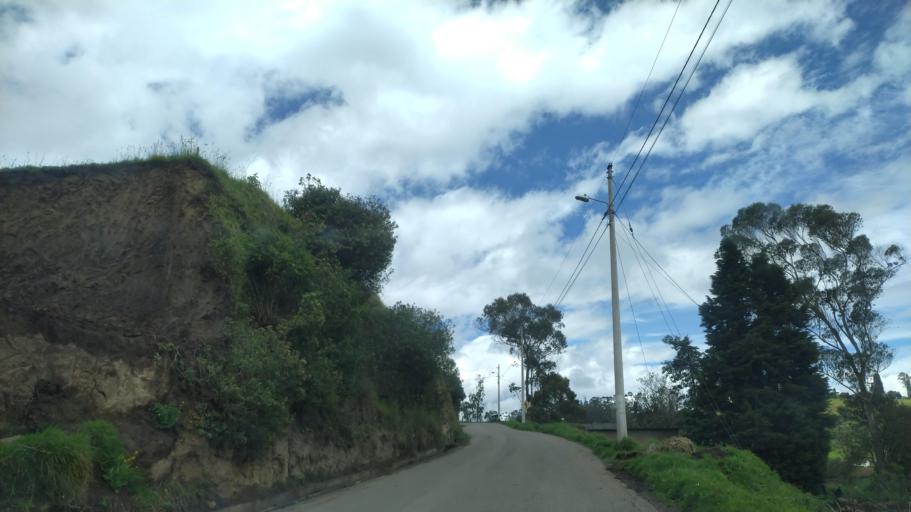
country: EC
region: Chimborazo
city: Riobamba
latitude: -1.6869
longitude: -78.5767
